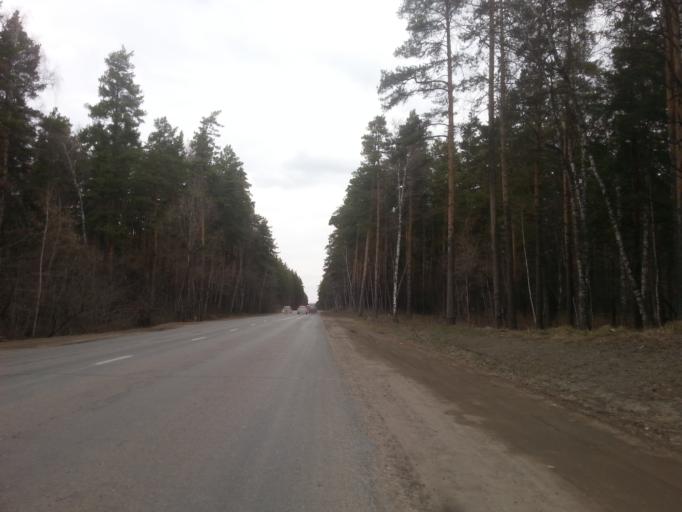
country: RU
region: Altai Krai
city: Yuzhnyy
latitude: 53.2792
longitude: 83.7180
